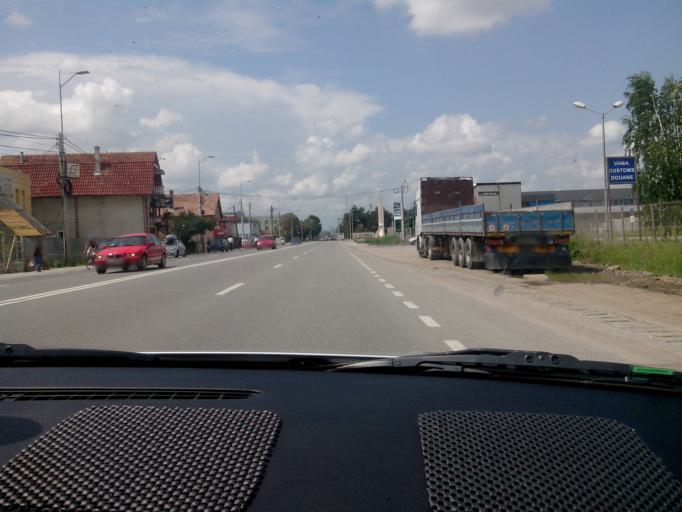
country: RO
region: Cluj
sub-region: Comuna Apahida
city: Sannicoara
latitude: 46.7822
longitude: 23.7005
